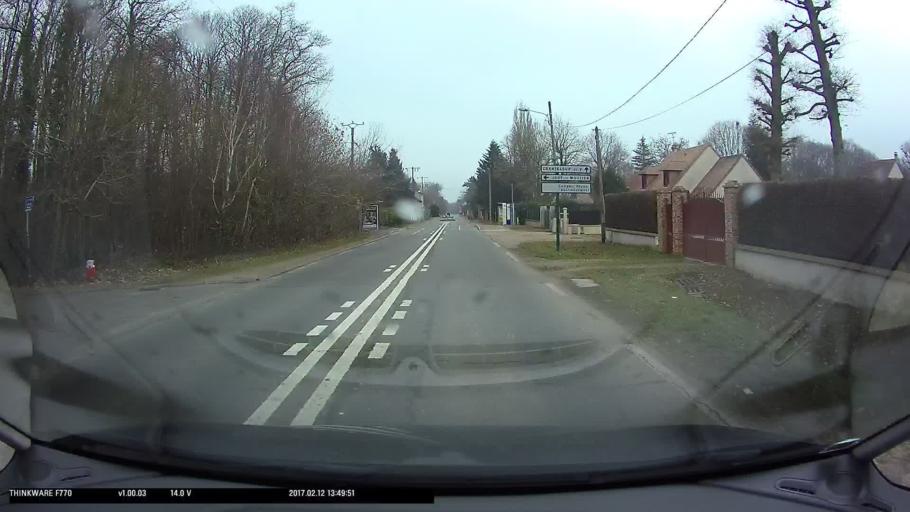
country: FR
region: Ile-de-France
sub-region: Departement des Yvelines
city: Triel-sur-Seine
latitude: 48.9975
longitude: 2.0168
